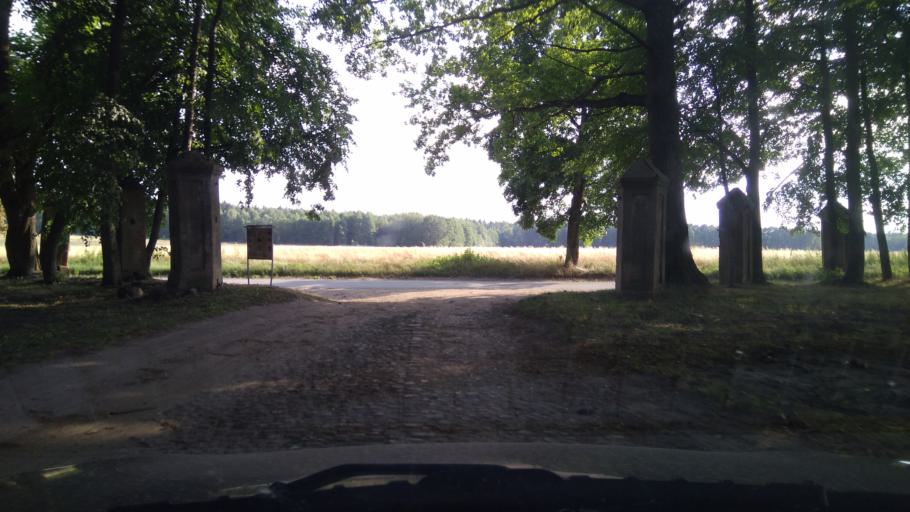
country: BY
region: Brest
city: Lyakhavichy
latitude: 53.0229
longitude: 26.3391
